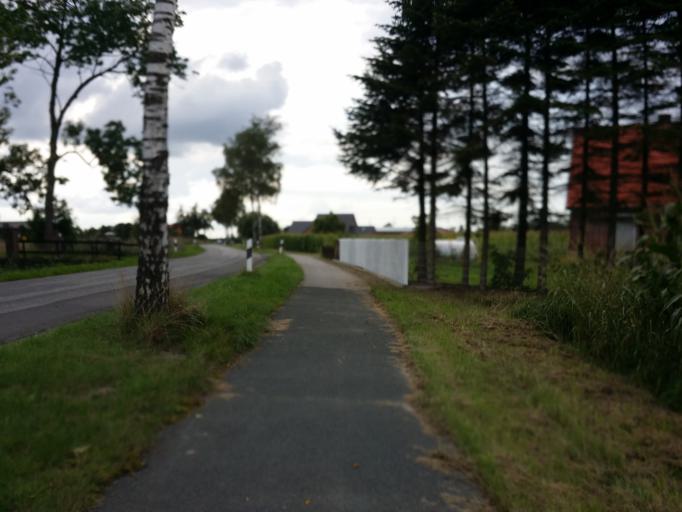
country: DE
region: Lower Saxony
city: Oederquart
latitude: 53.7849
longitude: 9.2347
